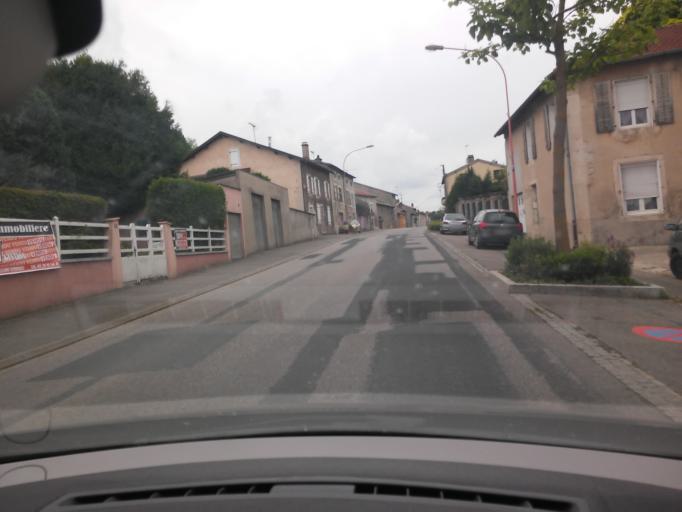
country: FR
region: Lorraine
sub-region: Departement de la Meuse
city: Lerouville
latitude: 48.7895
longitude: 5.5494
